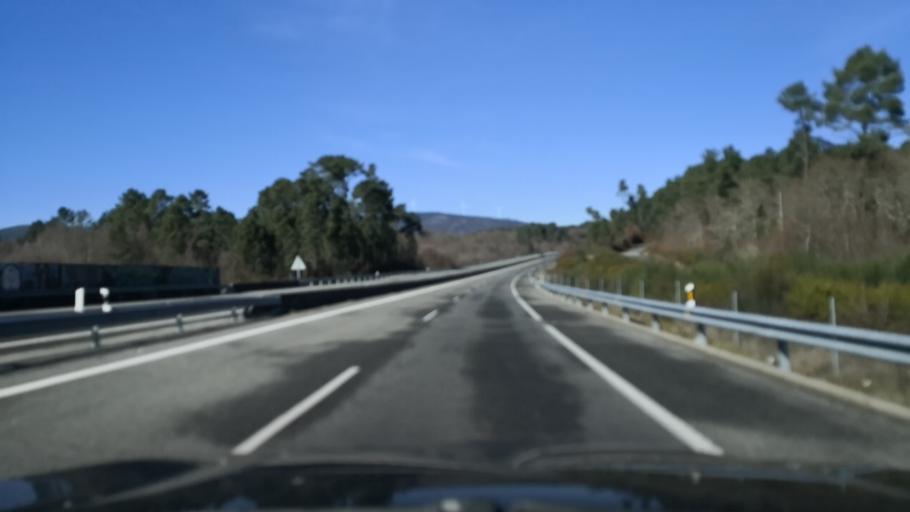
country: ES
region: Galicia
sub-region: Provincia de Ourense
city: Cea
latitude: 42.4647
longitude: -8.0268
